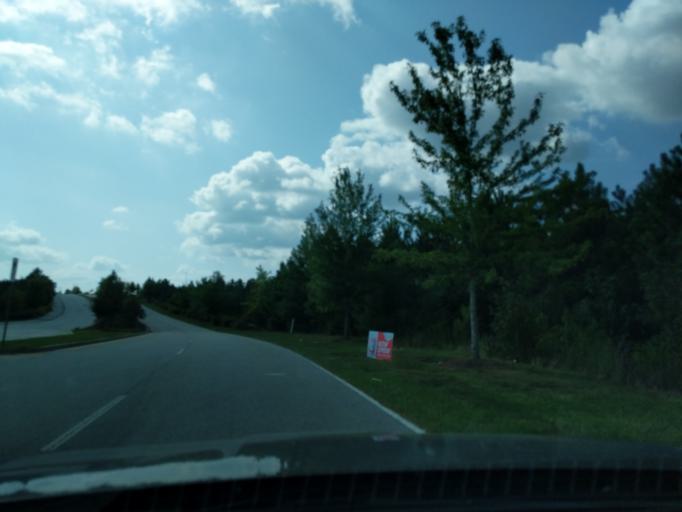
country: US
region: Georgia
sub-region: Columbia County
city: Grovetown
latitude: 33.4799
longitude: -82.1912
